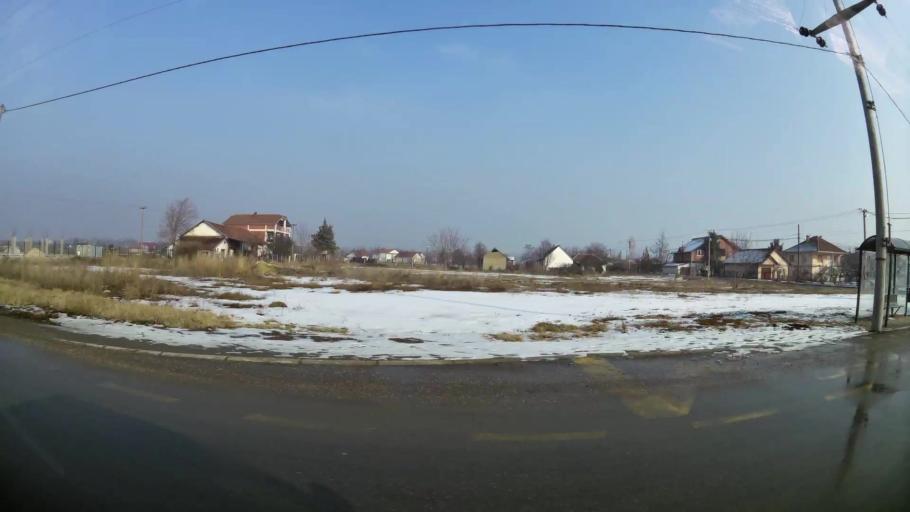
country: MK
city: Kadino
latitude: 41.9738
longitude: 21.5950
